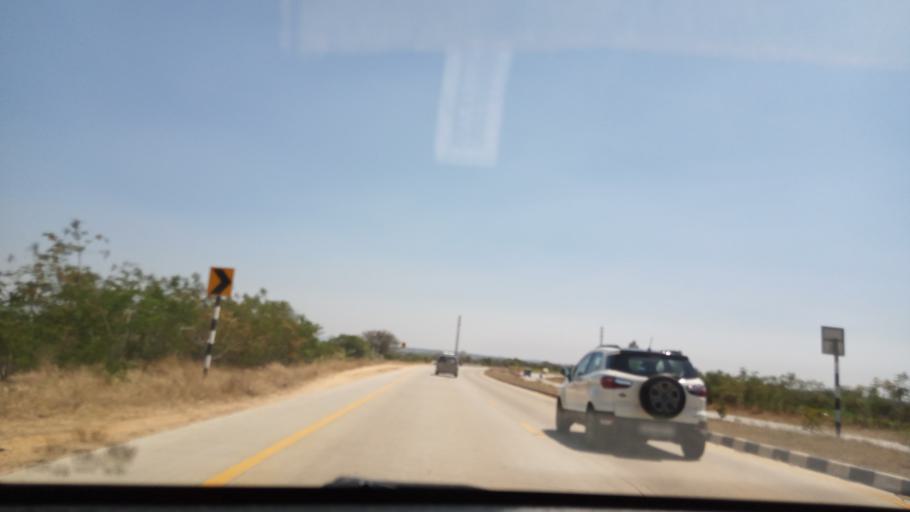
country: IN
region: Andhra Pradesh
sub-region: Chittoor
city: Palmaner
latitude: 13.1958
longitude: 78.6851
